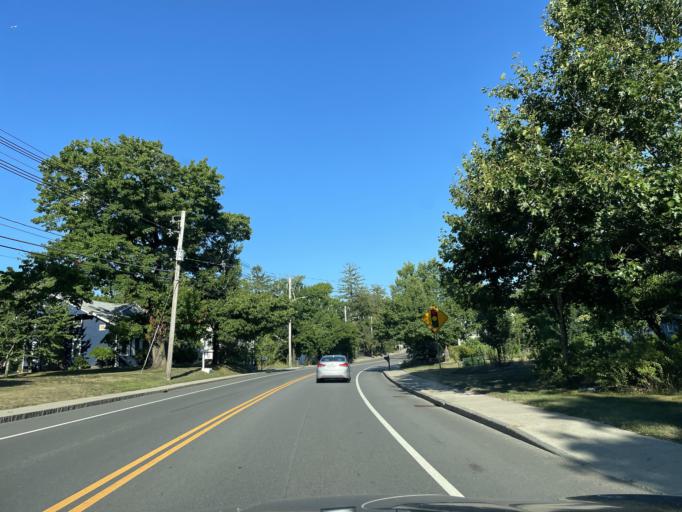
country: US
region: Massachusetts
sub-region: Bristol County
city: Mansfield
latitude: 42.0326
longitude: -71.1930
